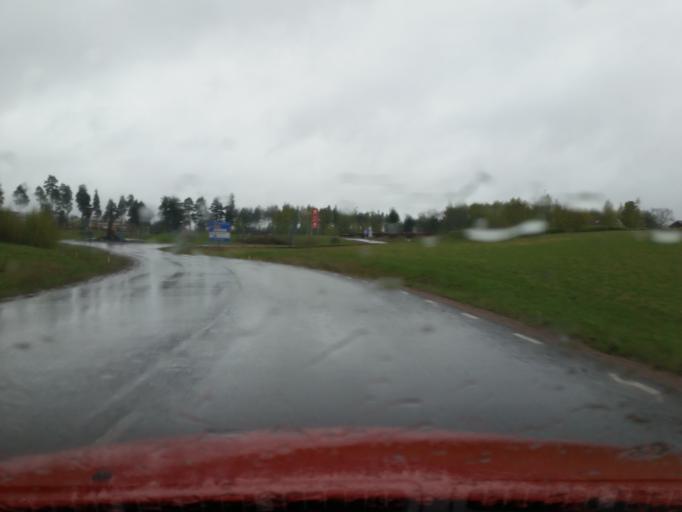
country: SE
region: Dalarna
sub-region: Leksand Municipality
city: Smedby
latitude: 60.6784
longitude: 15.0862
